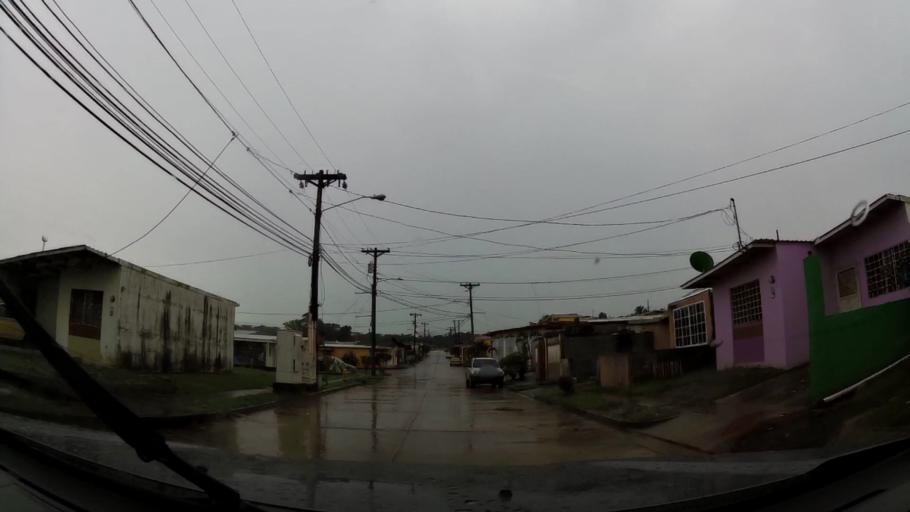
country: PA
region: Colon
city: Puerto Pilon
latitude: 9.3562
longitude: -79.7912
